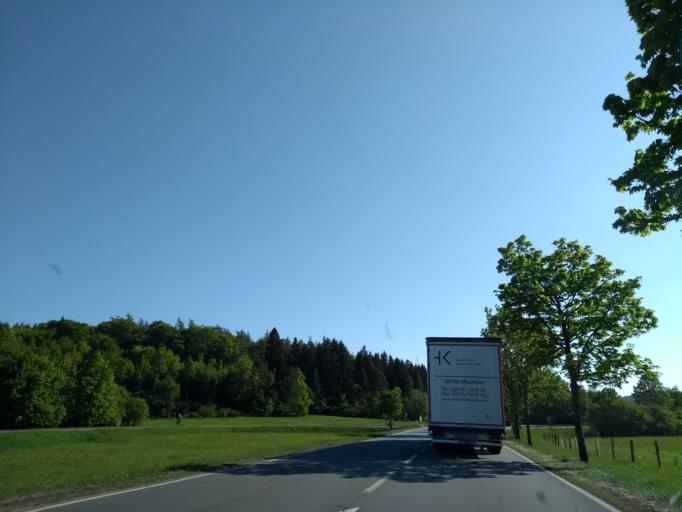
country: DE
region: Hesse
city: Battenberg
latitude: 50.9939
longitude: 8.6241
